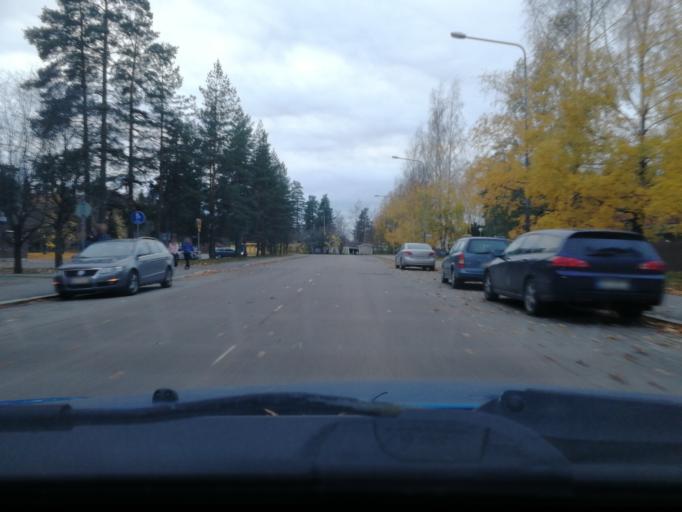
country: FI
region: Pirkanmaa
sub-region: Tampere
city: Tampere
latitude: 61.4565
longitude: 23.8375
